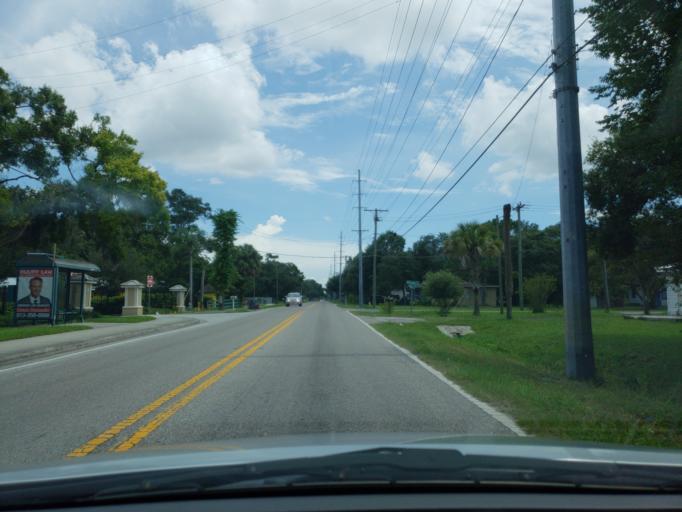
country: US
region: Florida
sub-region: Hillsborough County
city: East Lake-Orient Park
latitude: 27.9782
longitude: -82.3730
